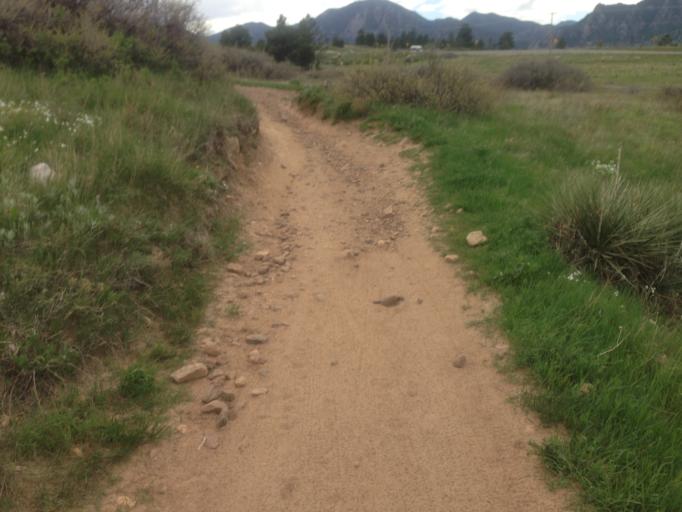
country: US
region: Colorado
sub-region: Boulder County
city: Superior
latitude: 39.9490
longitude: -105.2333
